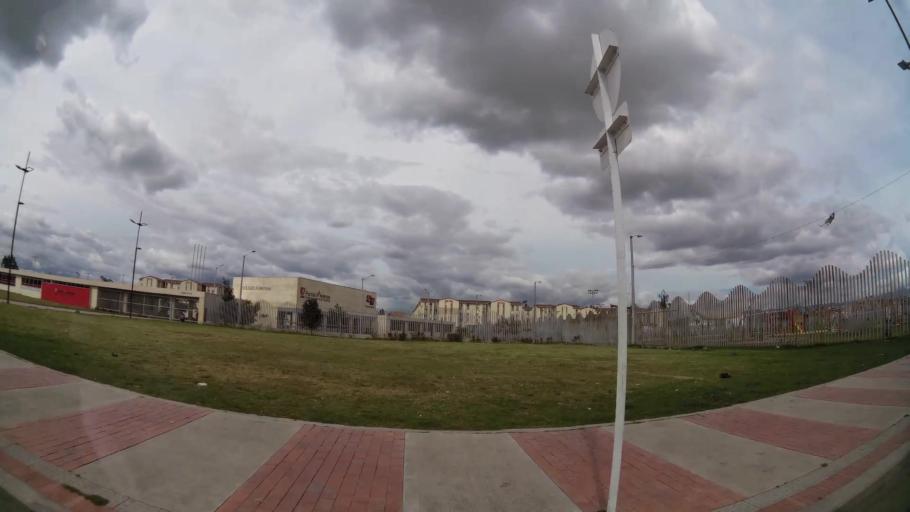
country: CO
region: Cundinamarca
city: Funza
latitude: 4.7115
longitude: -74.1984
